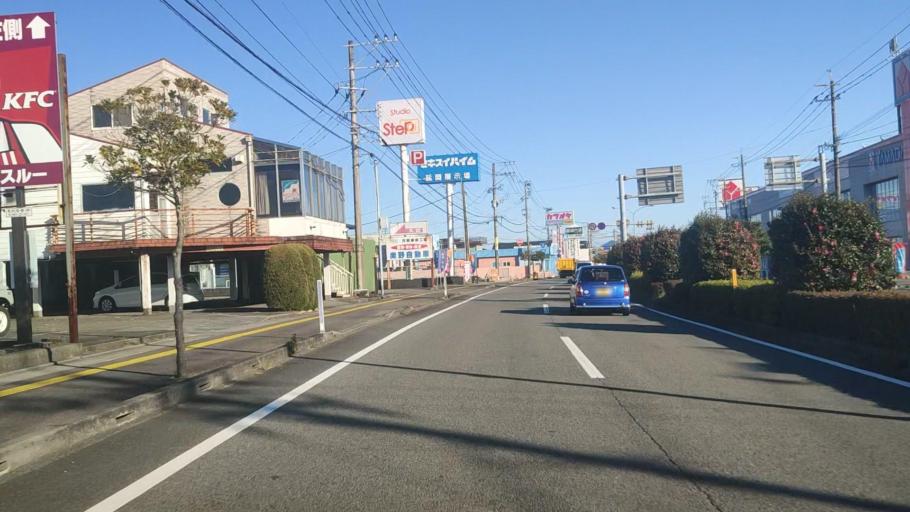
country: JP
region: Miyazaki
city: Nobeoka
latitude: 32.5494
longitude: 131.6771
